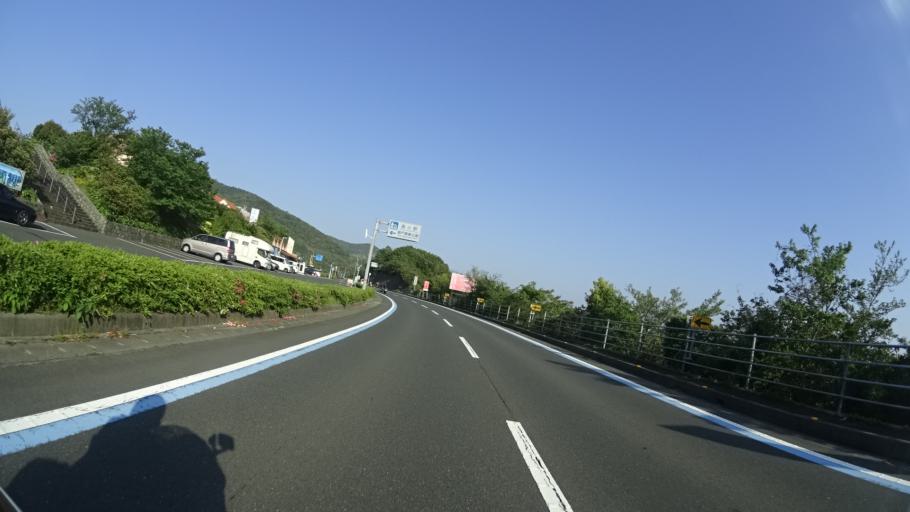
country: JP
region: Ehime
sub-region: Nishiuwa-gun
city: Ikata-cho
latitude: 33.4477
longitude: 132.2587
